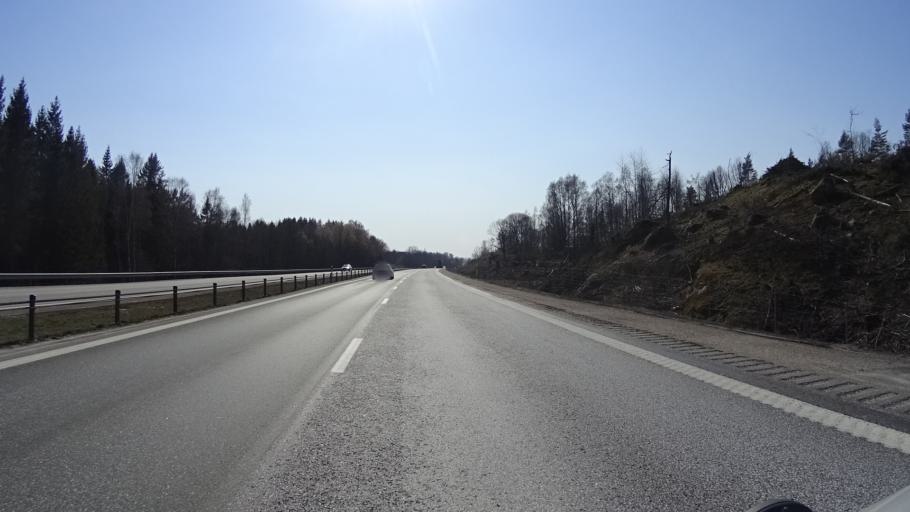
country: SE
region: OEstergoetland
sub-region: Odeshogs Kommun
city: OEdeshoeg
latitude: 58.1849
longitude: 14.6035
